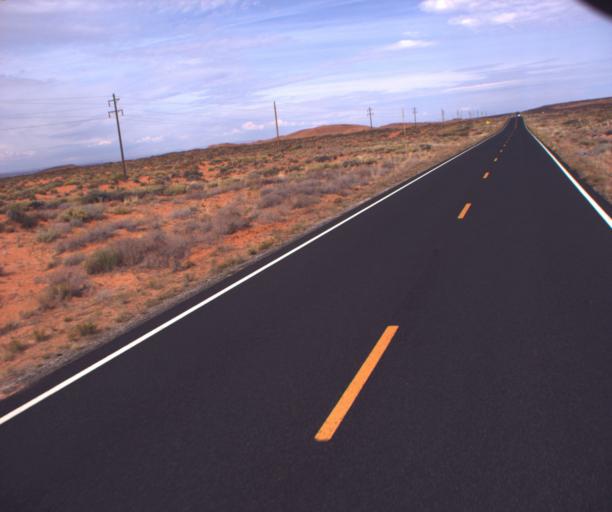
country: US
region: Arizona
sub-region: Apache County
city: Many Farms
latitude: 36.8659
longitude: -109.6338
